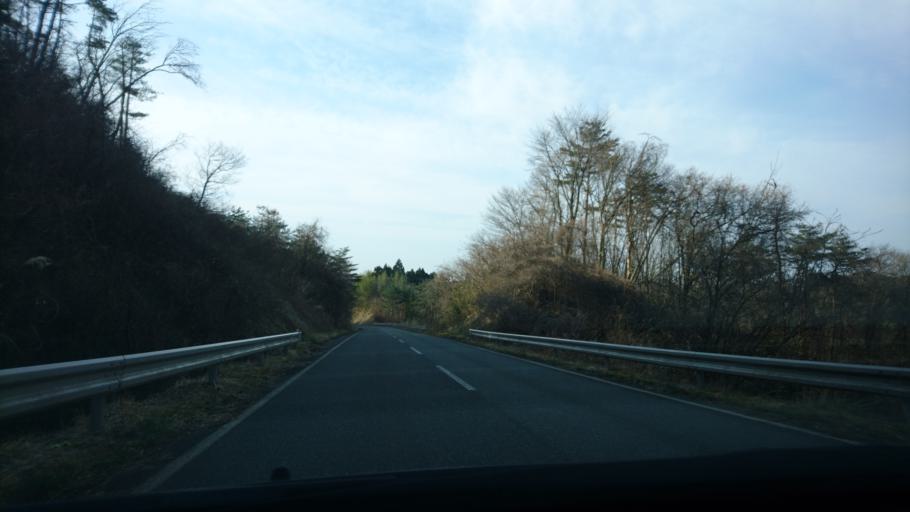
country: JP
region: Iwate
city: Ichinoseki
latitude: 38.8399
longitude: 141.2169
